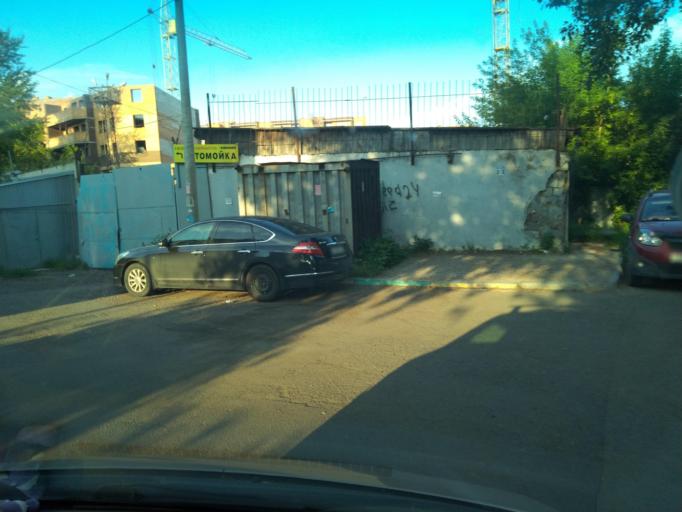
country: RU
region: Krasnoyarskiy
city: Krasnoyarsk
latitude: 56.0268
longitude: 92.8882
